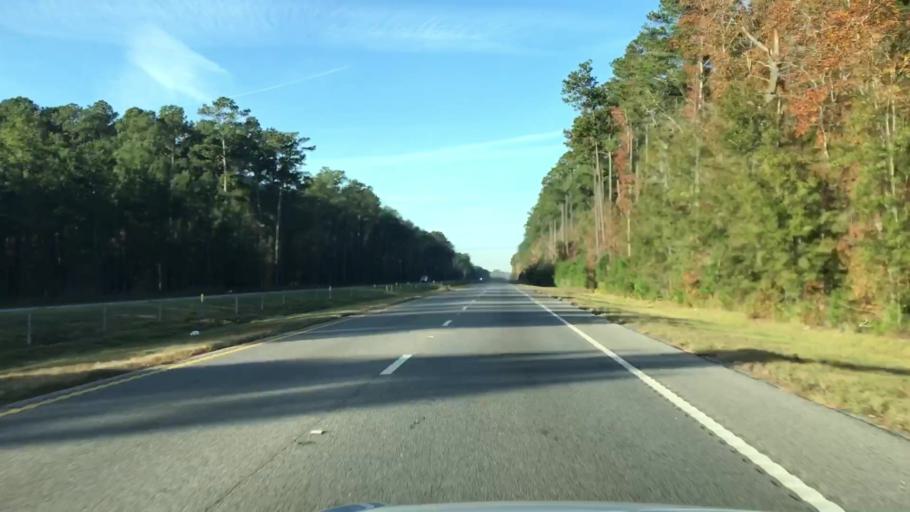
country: US
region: South Carolina
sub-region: Colleton County
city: Walterboro
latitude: 32.7663
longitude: -80.5006
